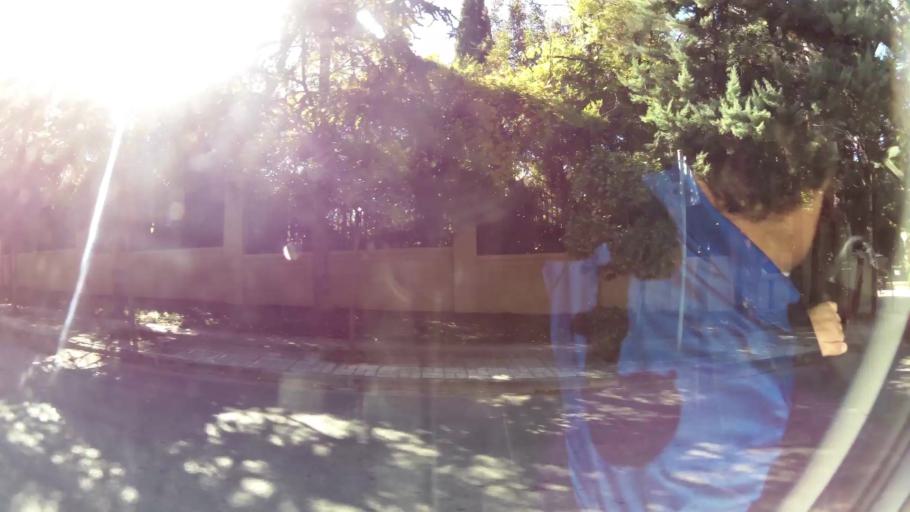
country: GR
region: Attica
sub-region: Nomarchia Athinas
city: Ekali
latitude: 38.1119
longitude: 23.8403
